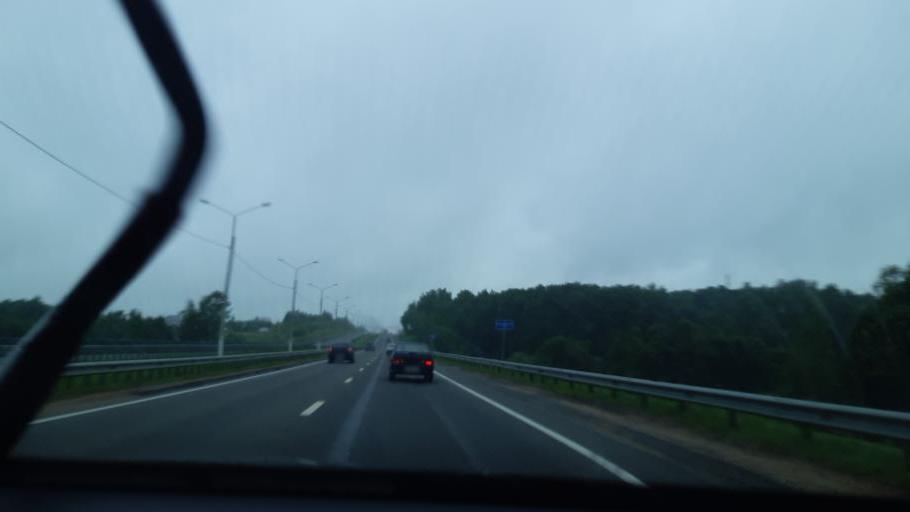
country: RU
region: Smolensk
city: Talashkino
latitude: 54.6755
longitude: 32.1455
